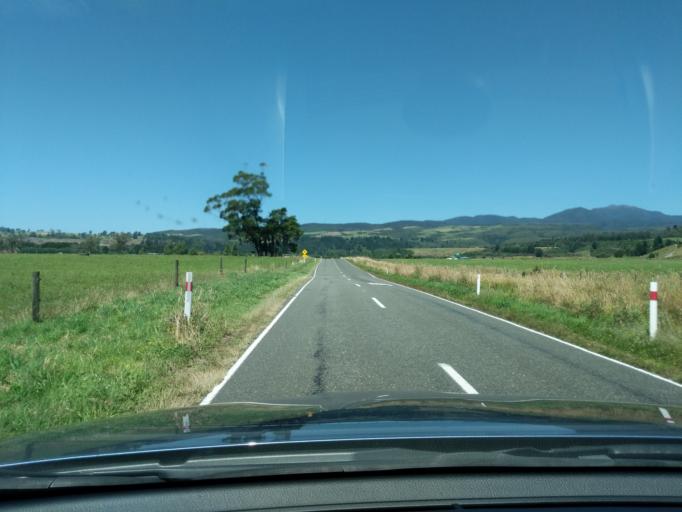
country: NZ
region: Tasman
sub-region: Tasman District
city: Takaka
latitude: -40.7282
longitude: 172.6106
